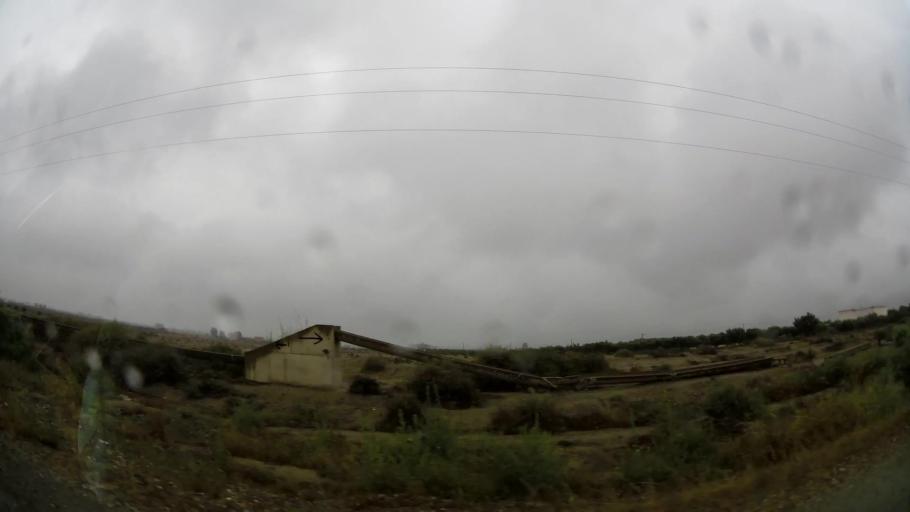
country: MA
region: Taza-Al Hoceima-Taounate
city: Imzourene
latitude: 35.1425
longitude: -3.8070
